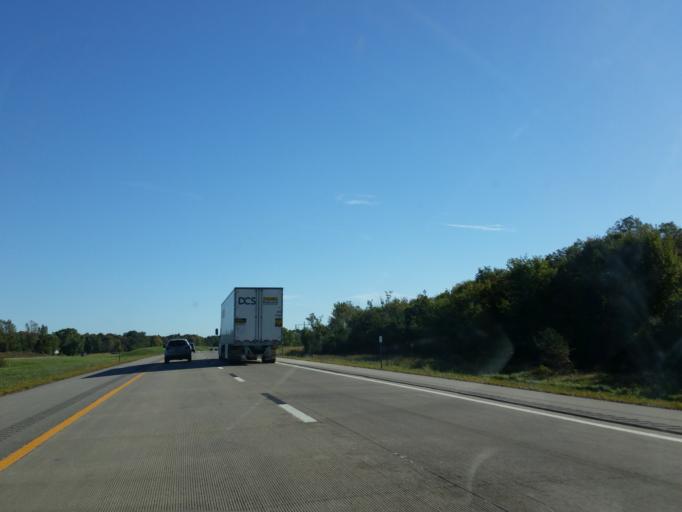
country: US
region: New York
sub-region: Erie County
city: Wanakah
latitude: 42.7253
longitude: -78.8810
